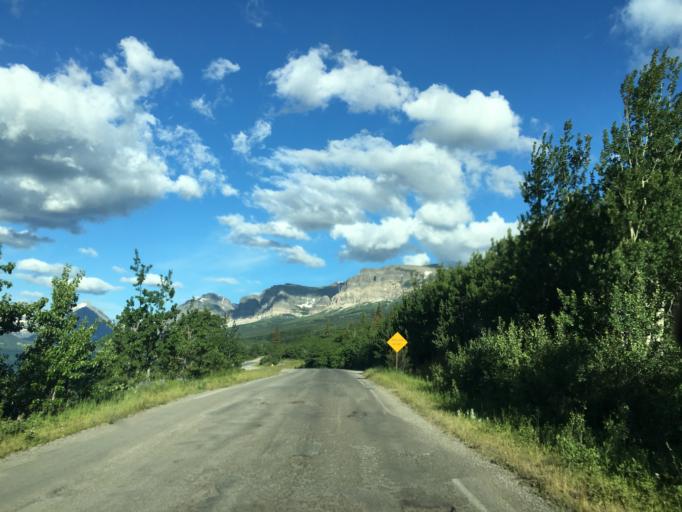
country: CA
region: Alberta
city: Cardston
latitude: 48.8301
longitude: -113.5305
